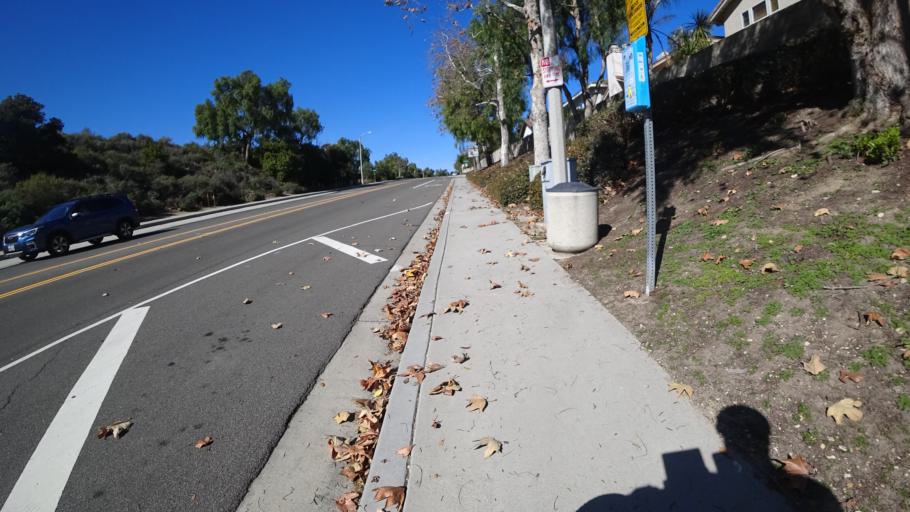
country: US
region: California
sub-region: Orange County
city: Aliso Viejo
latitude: 33.5511
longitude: -117.7294
